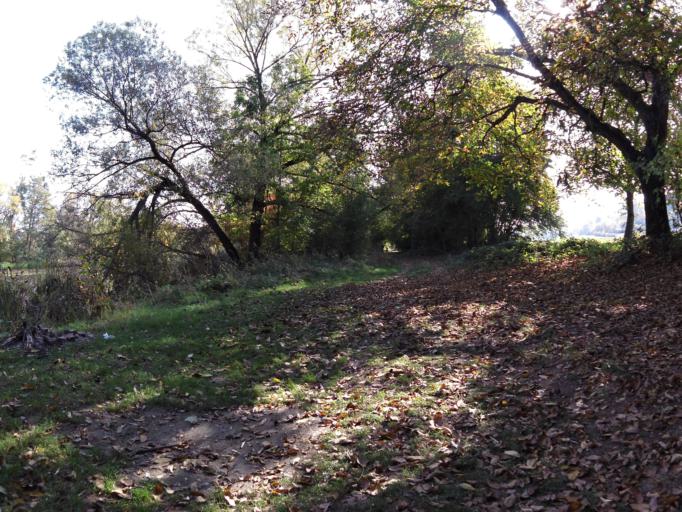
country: DE
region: Bavaria
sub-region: Regierungsbezirk Unterfranken
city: Eibelstadt
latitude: 49.7242
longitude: 9.9907
